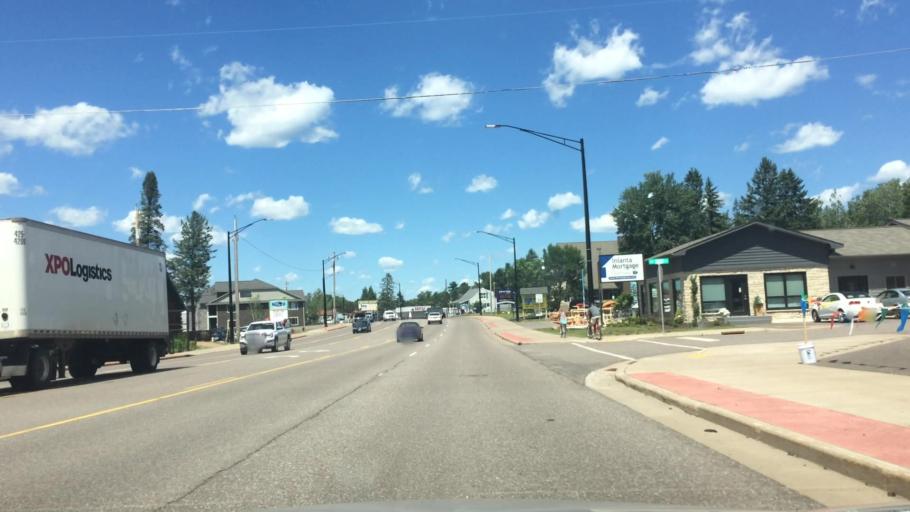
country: US
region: Wisconsin
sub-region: Vilas County
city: Lac du Flambeau
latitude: 45.8791
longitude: -89.7032
